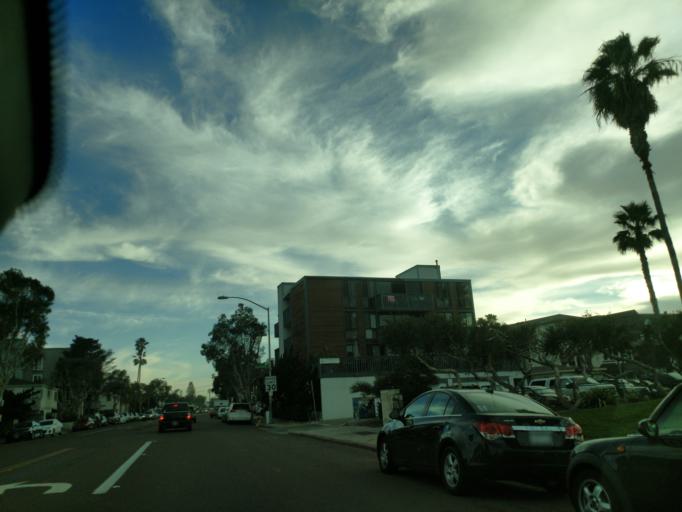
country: US
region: California
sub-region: San Diego County
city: La Jolla
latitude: 32.7681
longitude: -117.2511
